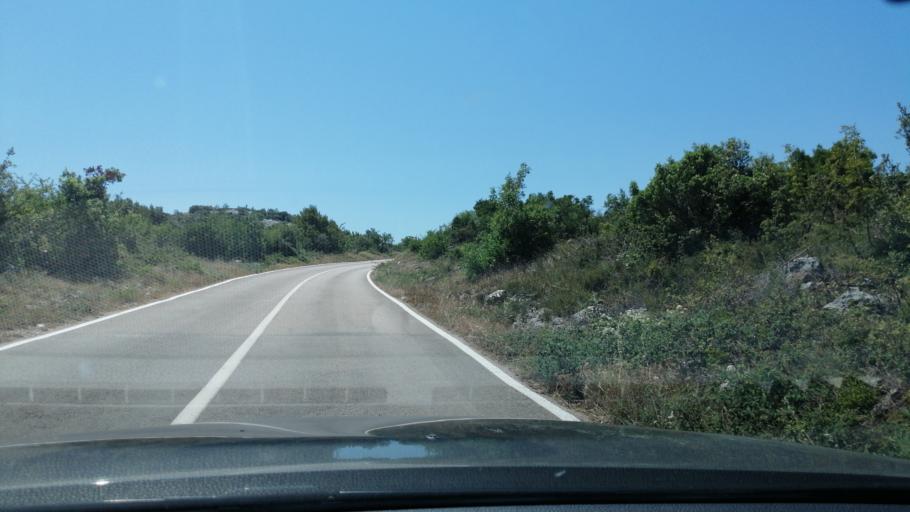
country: HR
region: Sibensko-Kniniska
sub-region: Grad Sibenik
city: Pirovac
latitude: 43.8585
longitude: 15.6928
